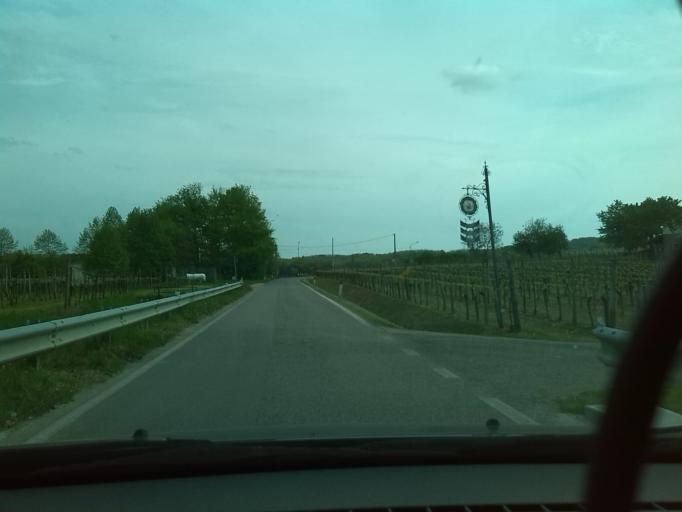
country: SI
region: Brda
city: Dobrovo
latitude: 45.9749
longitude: 13.4987
